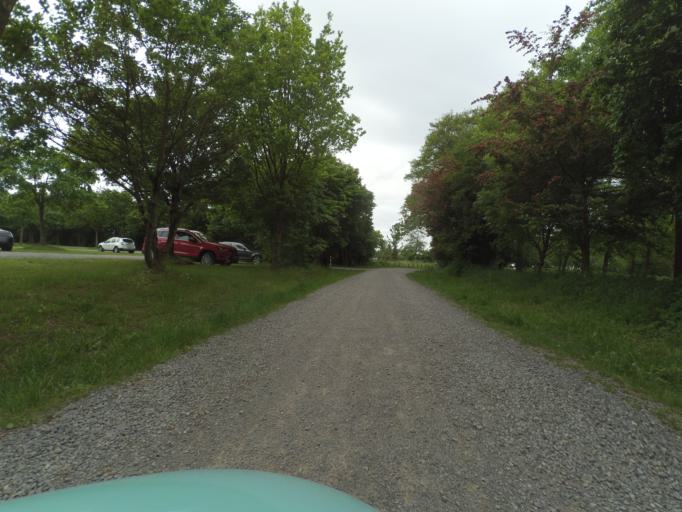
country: DE
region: Lower Saxony
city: Hagenburg
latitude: 52.4504
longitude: 9.3519
